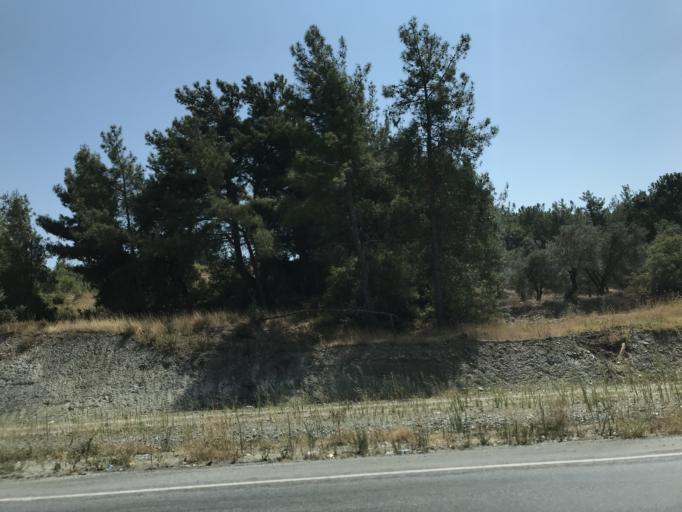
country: TR
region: Izmir
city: Selcuk
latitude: 37.8888
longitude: 27.3721
